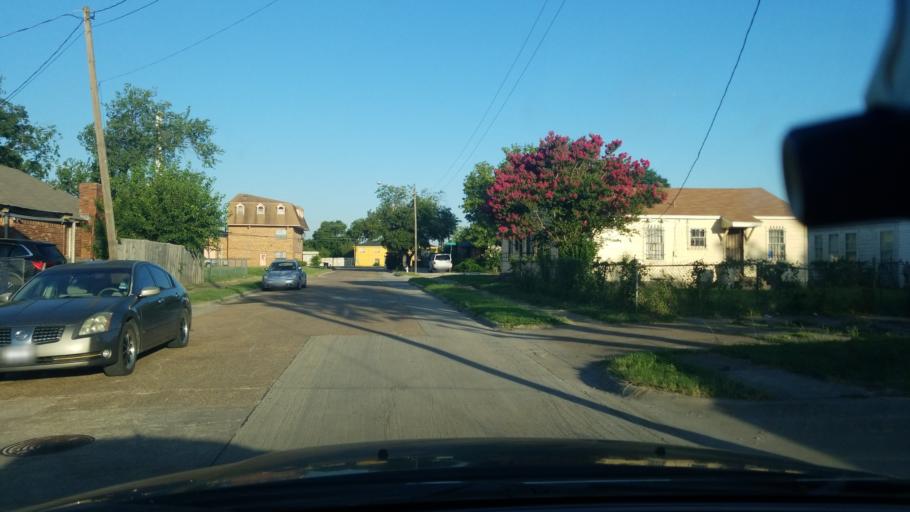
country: US
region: Texas
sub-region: Dallas County
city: Dallas
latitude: 32.7192
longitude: -96.8211
